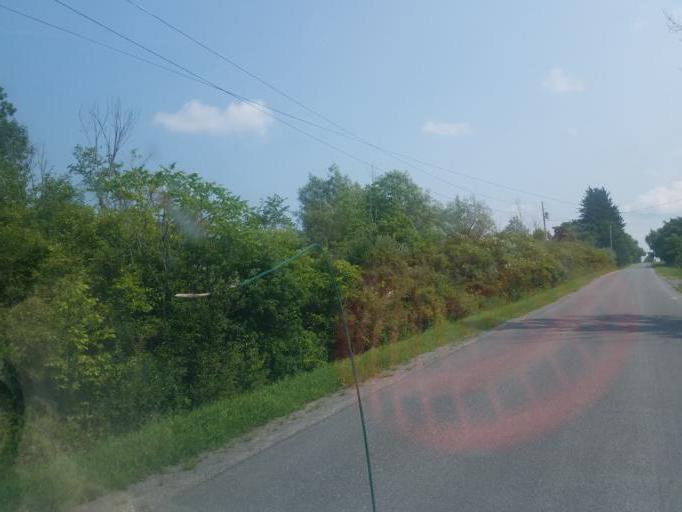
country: US
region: New York
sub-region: Montgomery County
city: Wellsville
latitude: 42.8576
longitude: -74.3573
